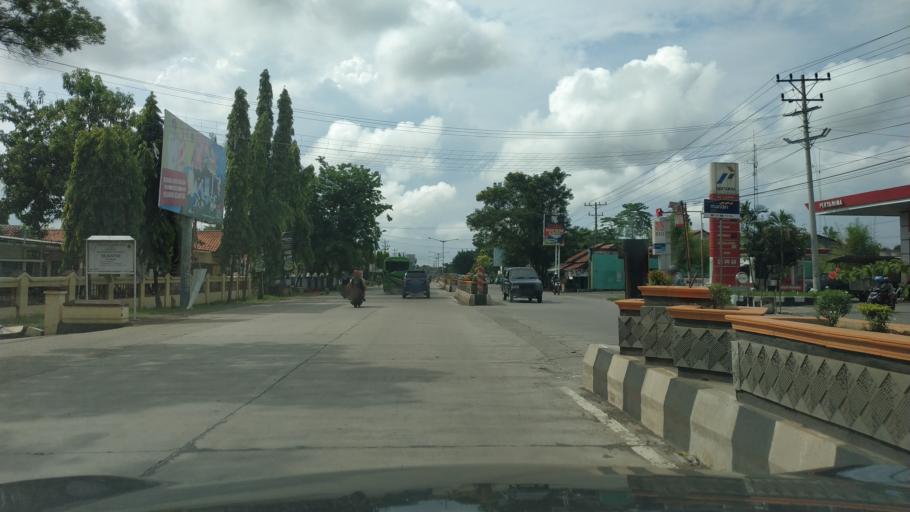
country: ID
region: Central Java
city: Pemalang
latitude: -6.9096
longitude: 109.3829
